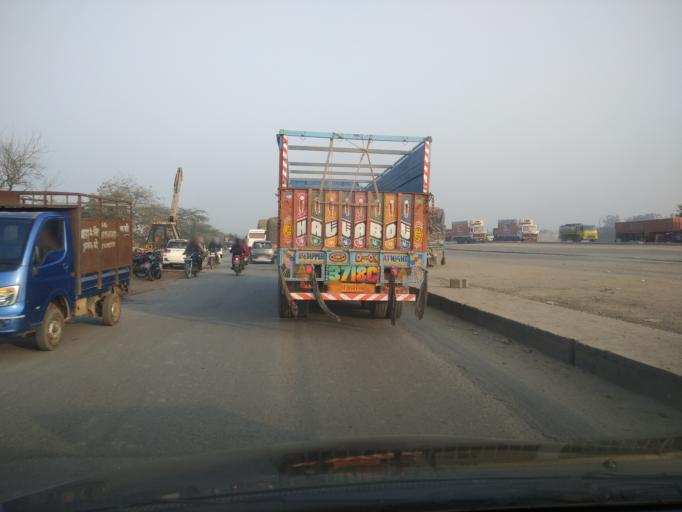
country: IN
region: Uttar Pradesh
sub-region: Varanasi
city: Ramnagar
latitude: 25.2521
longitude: 83.0650
